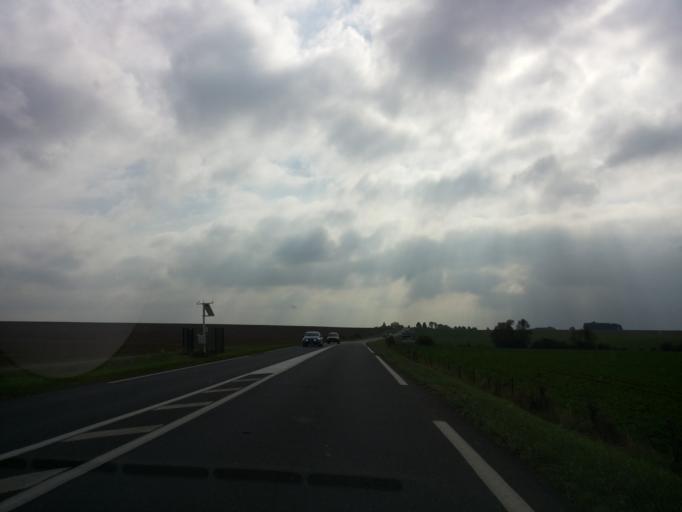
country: FR
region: Lorraine
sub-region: Departement de la Moselle
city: Solgne
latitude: 48.9914
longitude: 6.2839
